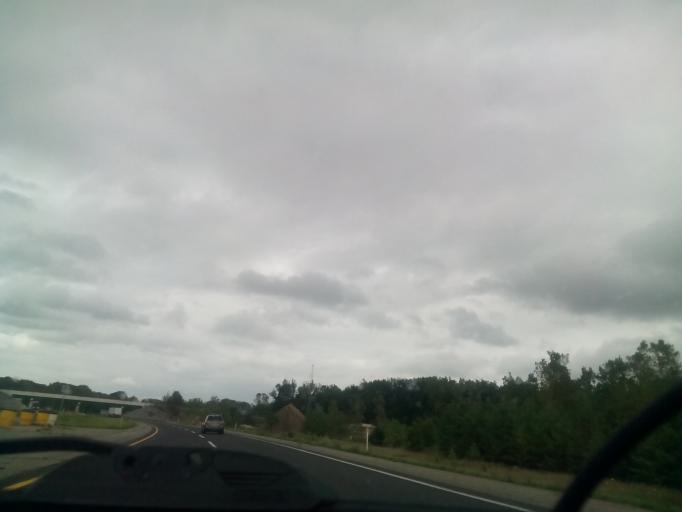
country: US
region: Indiana
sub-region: Steuben County
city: Hamilton
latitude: 41.6294
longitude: -84.8165
